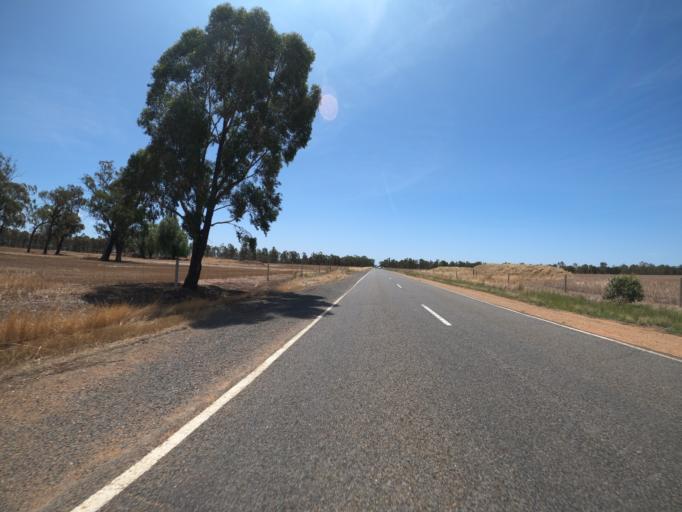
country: AU
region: Victoria
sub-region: Moira
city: Yarrawonga
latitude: -36.1645
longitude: 145.9672
